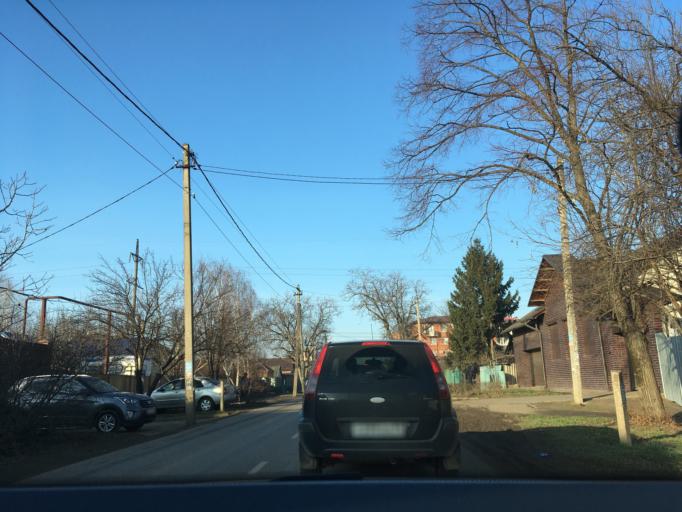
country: RU
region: Krasnodarskiy
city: Krasnodar
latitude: 45.0781
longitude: 39.0208
